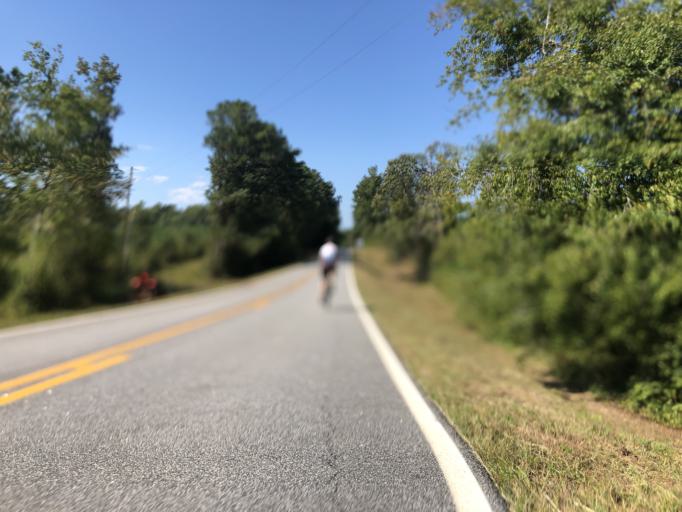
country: US
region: Georgia
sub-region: Coweta County
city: Newnan
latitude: 33.4059
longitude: -84.9524
